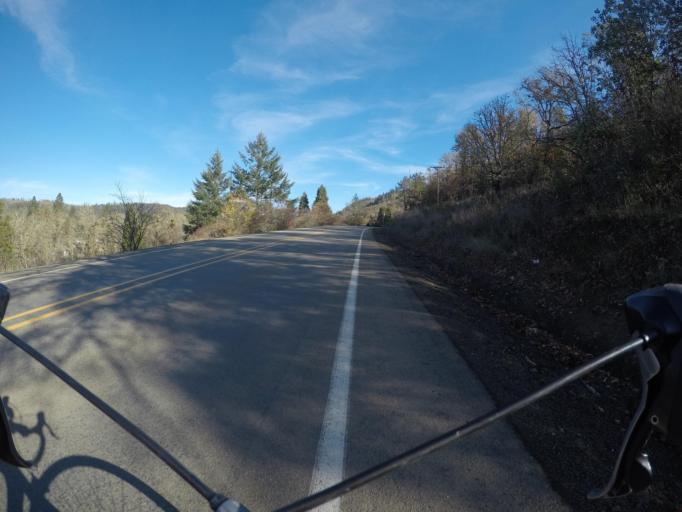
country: US
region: Oregon
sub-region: Douglas County
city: Winston
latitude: 43.1867
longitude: -123.4583
